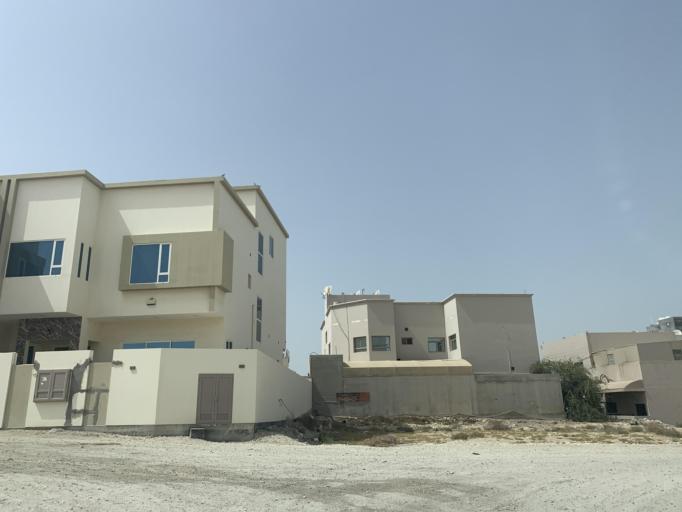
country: BH
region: Northern
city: Madinat `Isa
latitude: 26.1558
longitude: 50.5157
